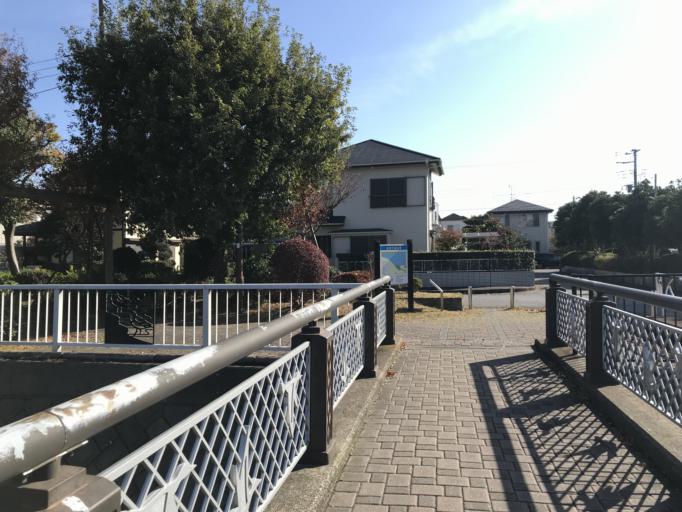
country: JP
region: Chiba
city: Funabashi
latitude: 35.6742
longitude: 140.0086
